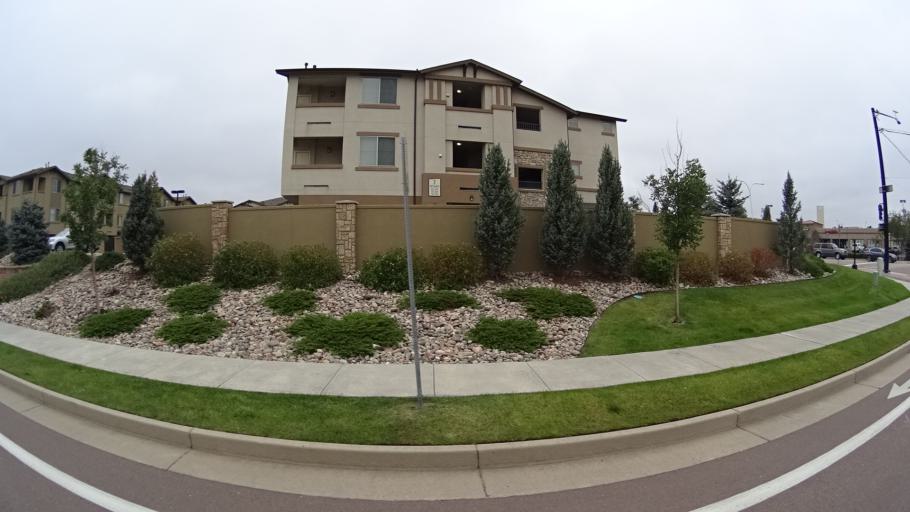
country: US
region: Colorado
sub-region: El Paso County
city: Cimarron Hills
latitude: 38.8854
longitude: -104.7130
